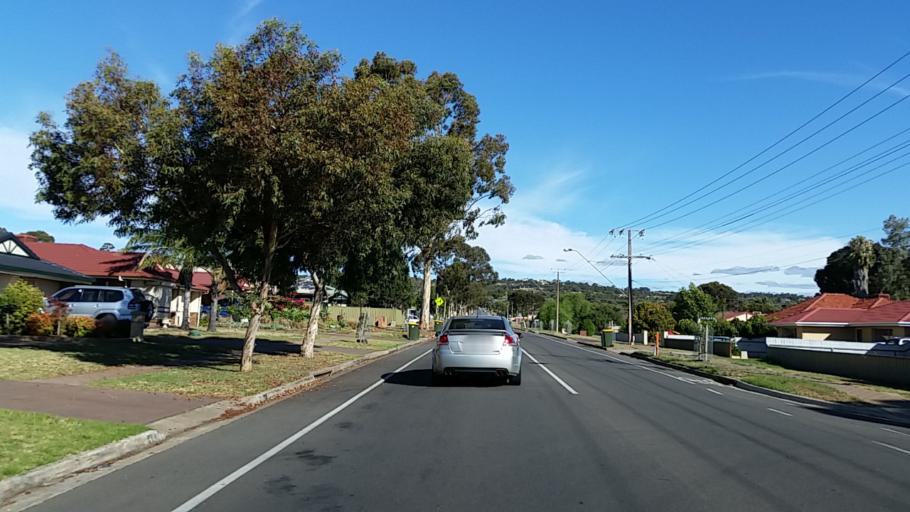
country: AU
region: South Australia
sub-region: Salisbury
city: Salisbury
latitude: -34.7860
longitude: 138.6590
